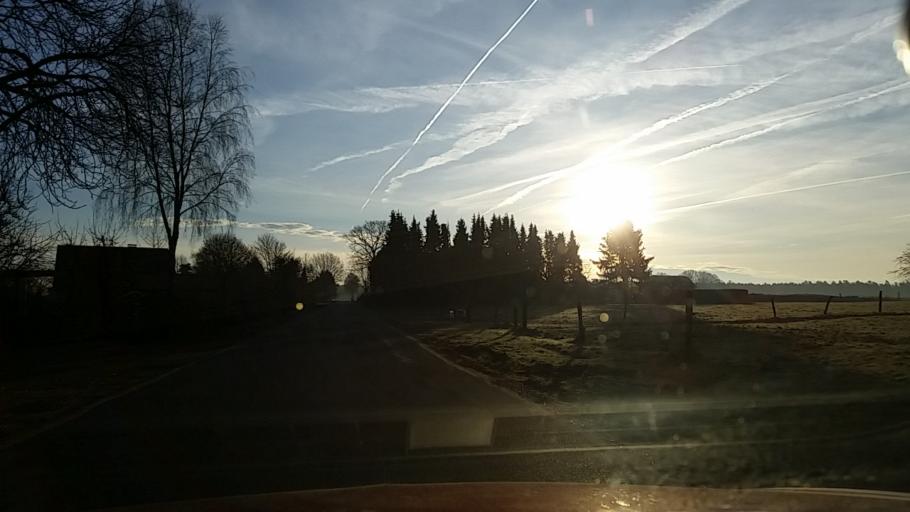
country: DE
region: Lower Saxony
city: Dedelstorf
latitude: 52.7320
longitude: 10.5174
